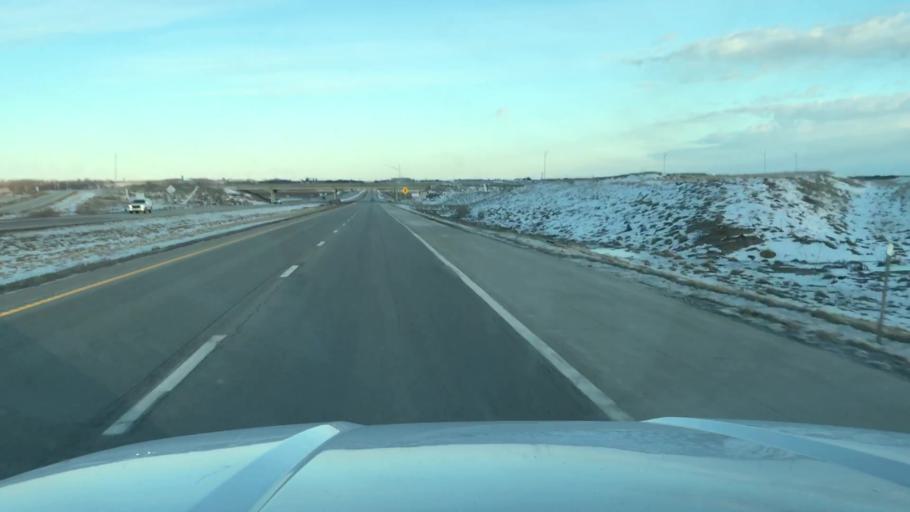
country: US
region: Missouri
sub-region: Buchanan County
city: Saint Joseph
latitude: 39.7480
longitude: -94.7540
